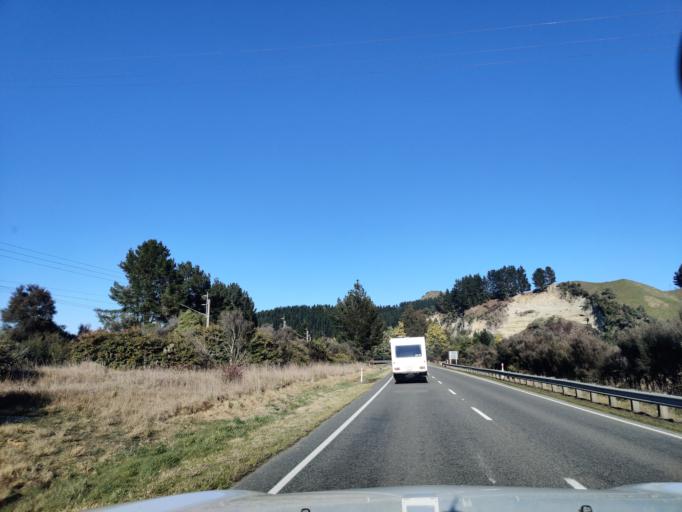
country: NZ
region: Manawatu-Wanganui
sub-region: Ruapehu District
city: Waiouru
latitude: -39.7539
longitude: 175.8315
